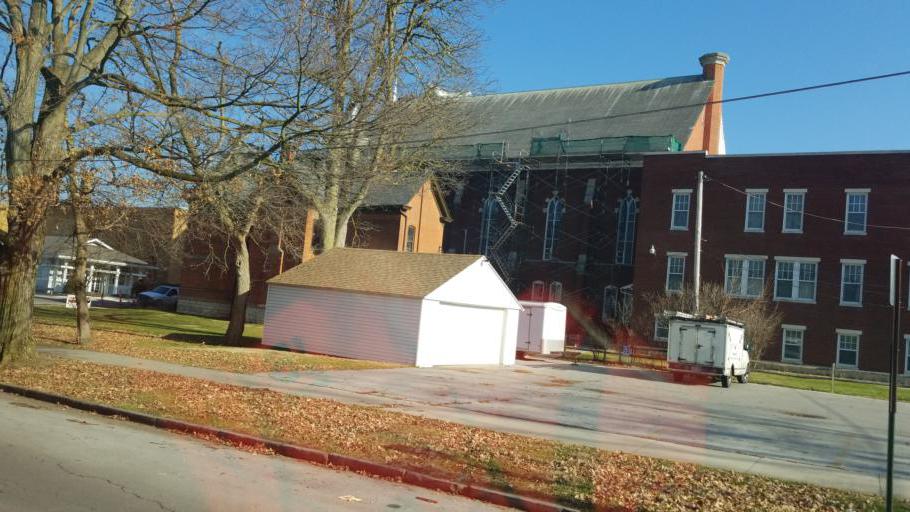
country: US
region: Ohio
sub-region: Seneca County
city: Tiffin
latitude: 41.1127
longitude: -83.1779
